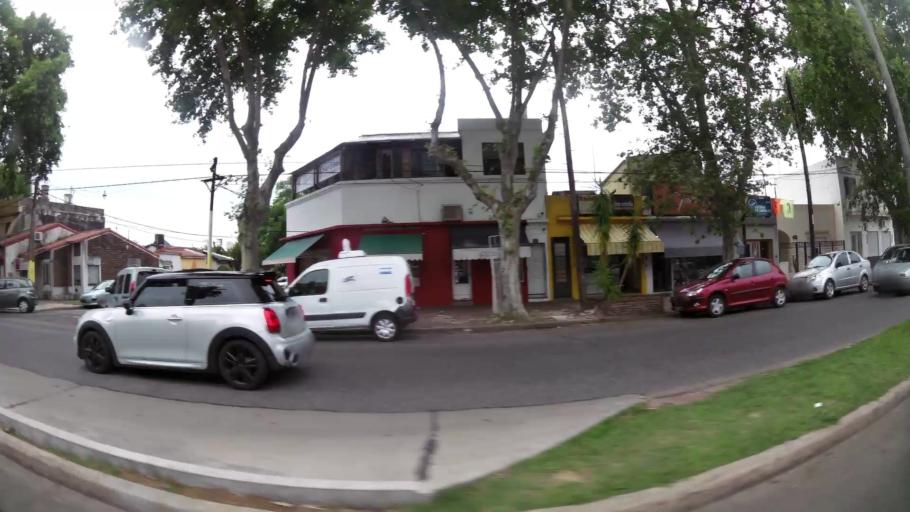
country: AR
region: Santa Fe
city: Granadero Baigorria
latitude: -32.8853
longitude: -60.6951
